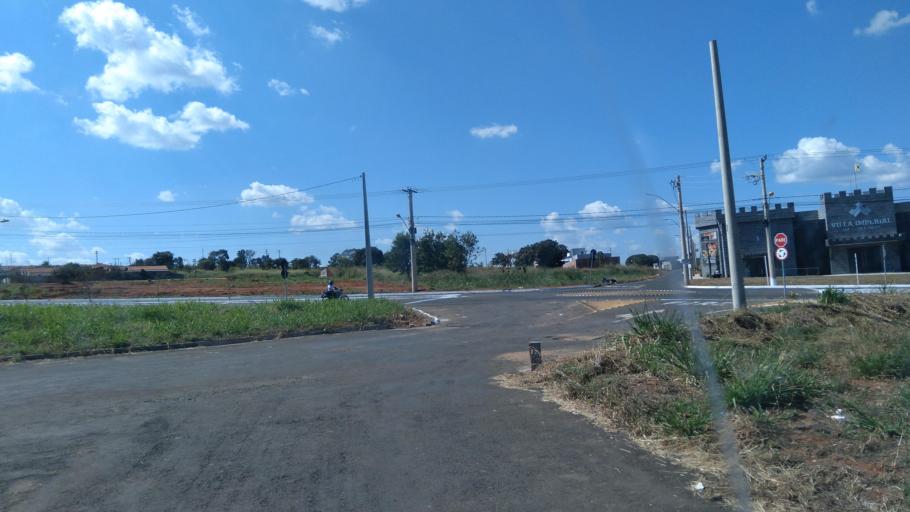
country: BR
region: Goias
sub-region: Mineiros
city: Mineiros
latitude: -17.5529
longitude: -52.5412
